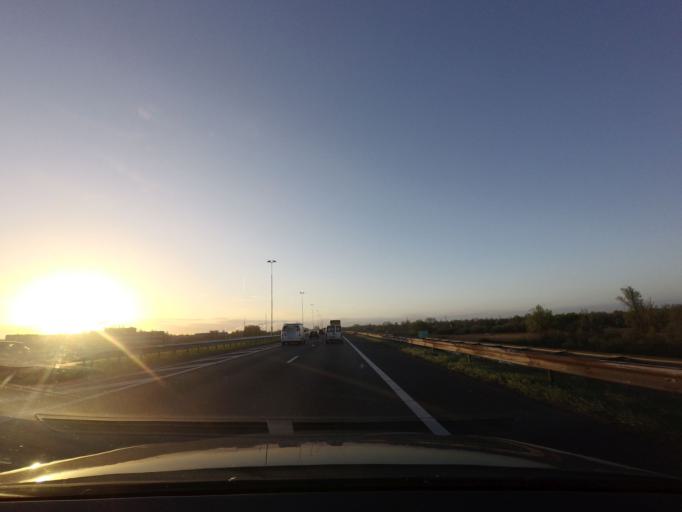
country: NL
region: North Holland
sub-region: Gemeente Zaanstad
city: Zaanstad
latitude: 52.4680
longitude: 4.7917
